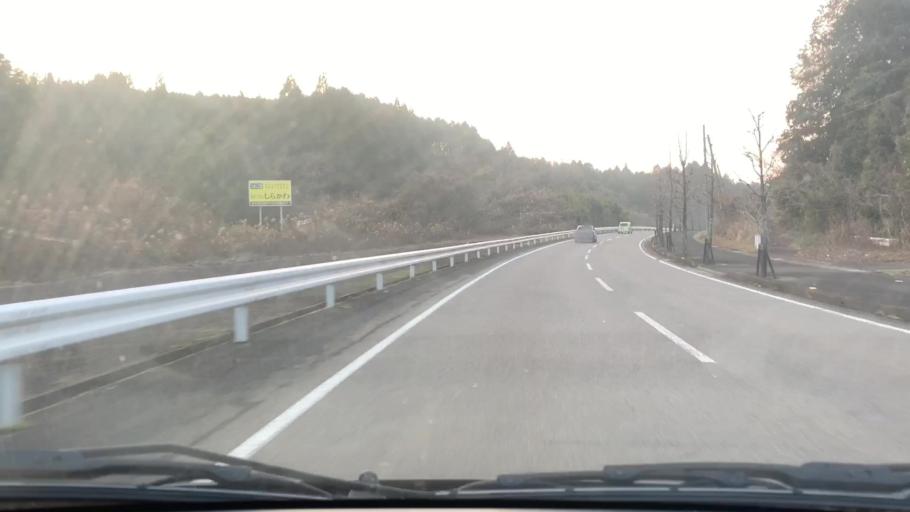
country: JP
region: Saga Prefecture
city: Imaricho-ko
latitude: 33.2592
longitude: 129.9246
